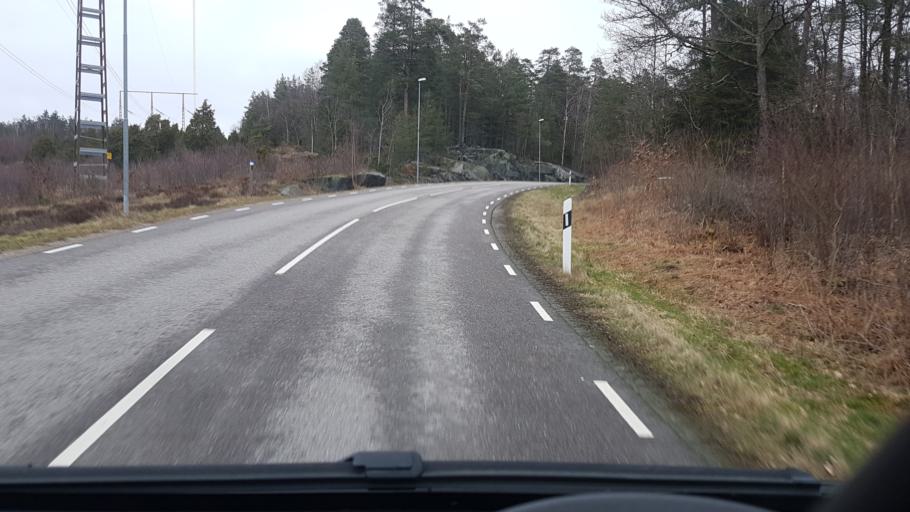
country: SE
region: Vaestra Goetaland
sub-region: Lerums Kommun
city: Stenkullen
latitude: 57.8086
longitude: 12.3347
